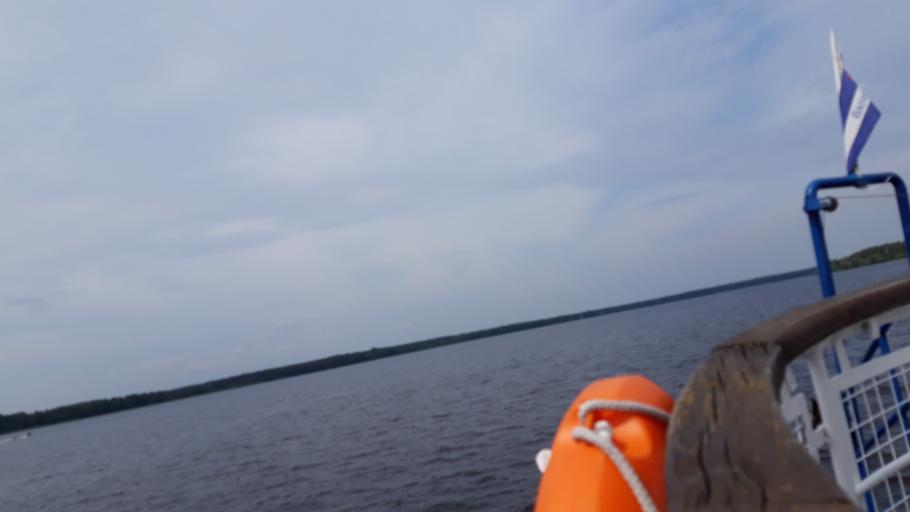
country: RU
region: Tverskaya
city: Konakovo
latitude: 56.7557
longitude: 36.7435
